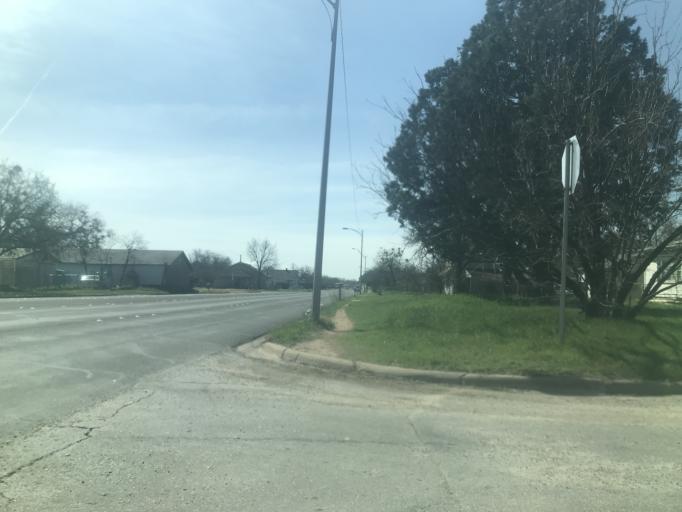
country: US
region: Texas
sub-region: Taylor County
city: Abilene
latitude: 32.4691
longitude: -99.7397
